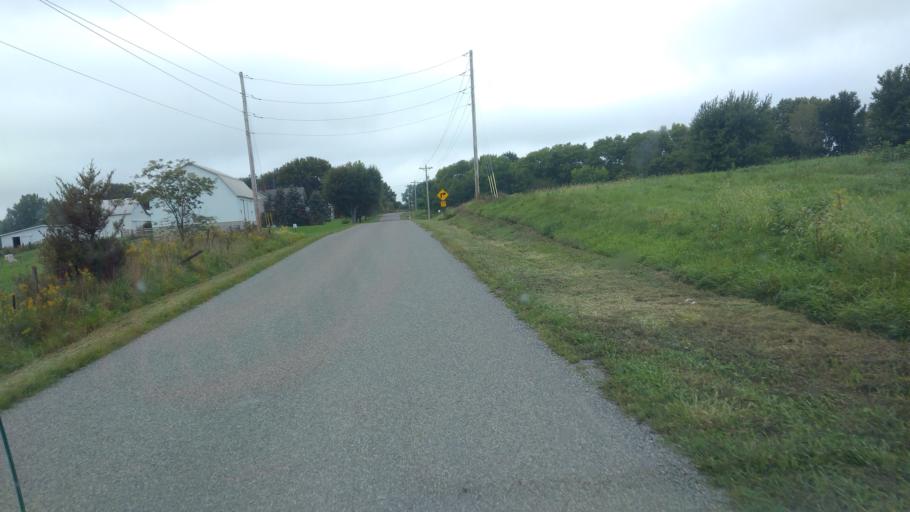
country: US
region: Ohio
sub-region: Hardin County
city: Kenton
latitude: 40.5768
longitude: -83.6768
